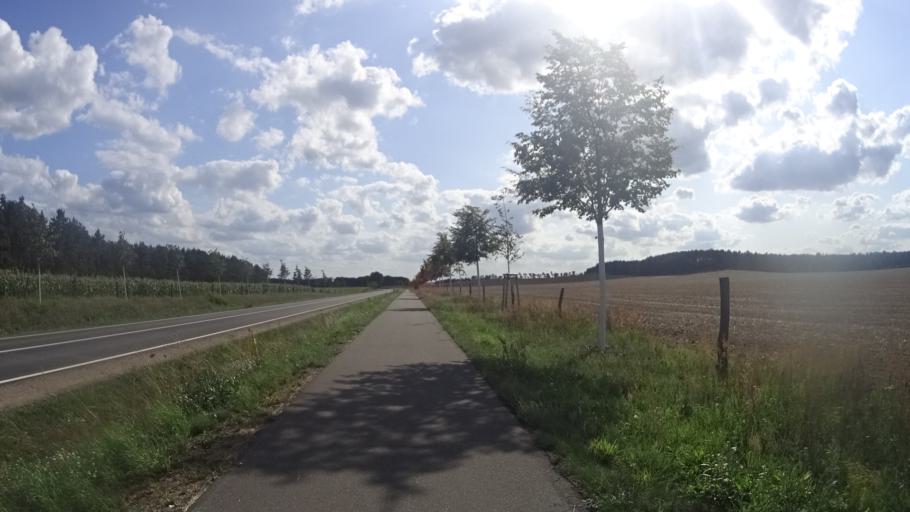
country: DE
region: Brandenburg
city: Rhinow
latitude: 52.7004
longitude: 12.3699
